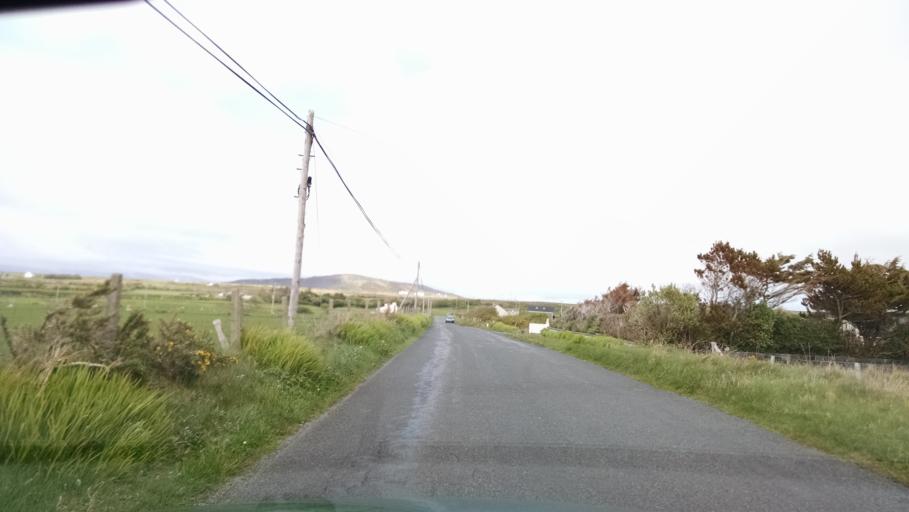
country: IE
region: Connaught
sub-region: County Galway
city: Clifden
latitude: 53.7282
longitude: -9.8674
